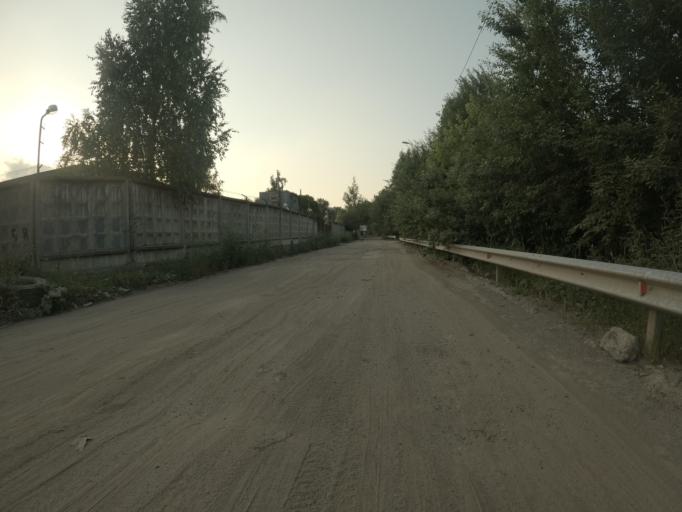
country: RU
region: St.-Petersburg
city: Krasnogvargeisky
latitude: 59.9581
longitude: 30.4568
